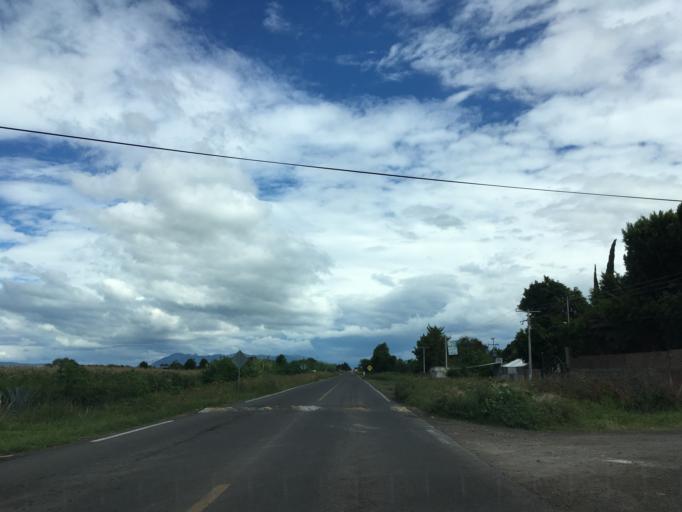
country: MX
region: Michoacan
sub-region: Cuitzeo
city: Cuamio
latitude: 20.0691
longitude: -101.1160
